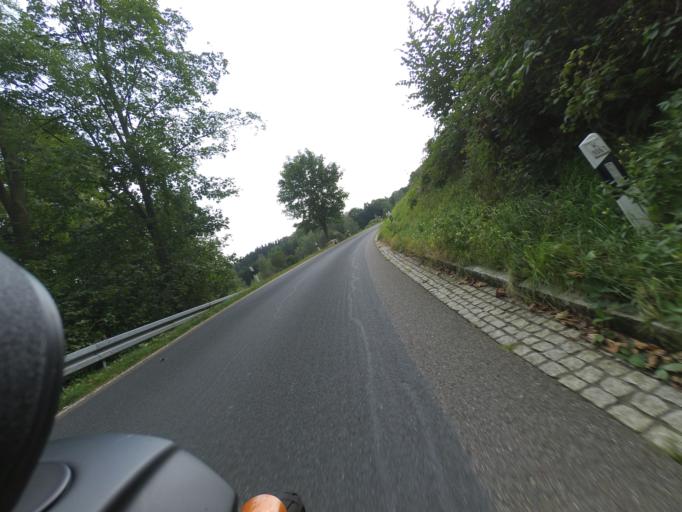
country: DE
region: Saxony
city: Barenstein
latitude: 50.8185
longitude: 13.8249
